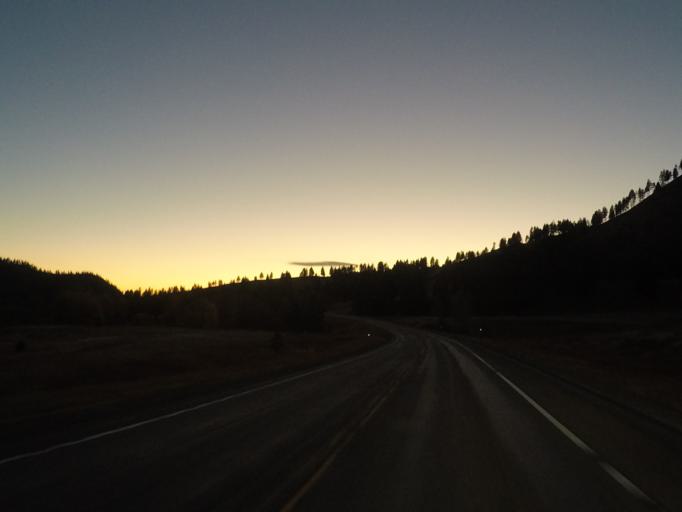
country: US
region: Montana
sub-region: Missoula County
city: Seeley Lake
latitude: 47.0302
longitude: -113.2770
